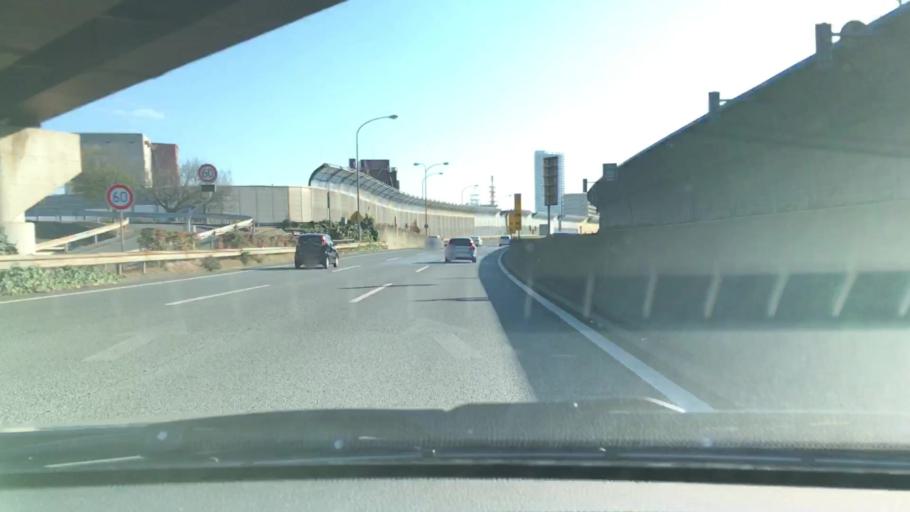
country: JP
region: Chiba
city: Funabashi
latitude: 35.6991
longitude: 139.9682
